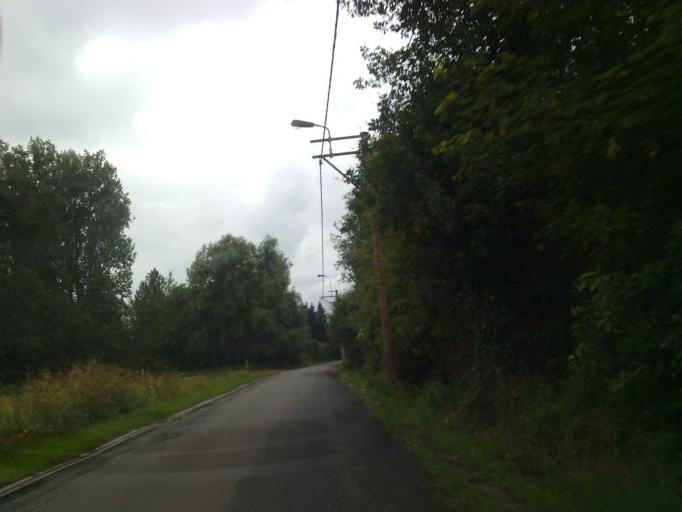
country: BE
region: Flanders
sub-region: Provincie Oost-Vlaanderen
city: Berlare
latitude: 51.0293
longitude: 3.9827
